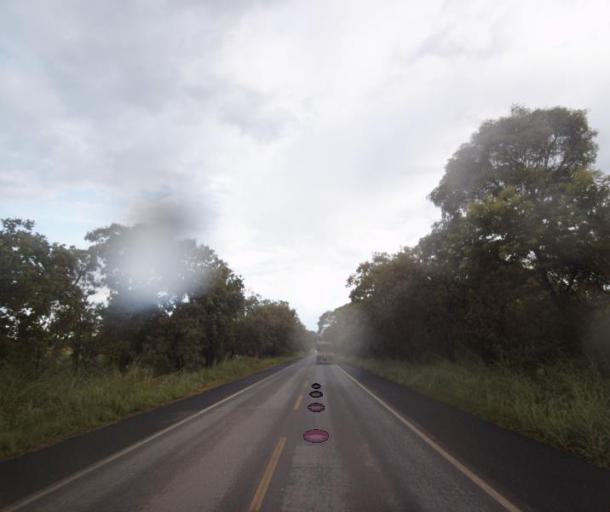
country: BR
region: Goias
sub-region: Porangatu
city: Porangatu
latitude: -13.9051
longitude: -49.0625
